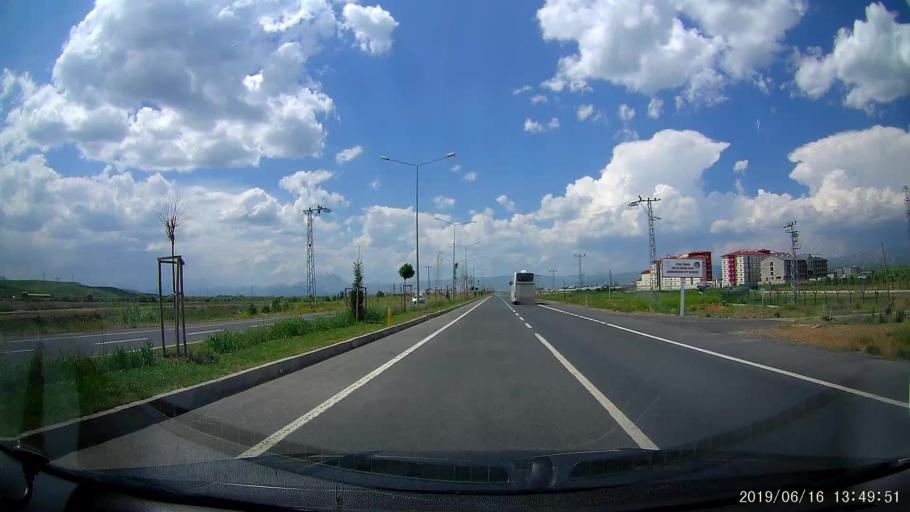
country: TR
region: Agri
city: Agri
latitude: 39.7209
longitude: 42.9859
